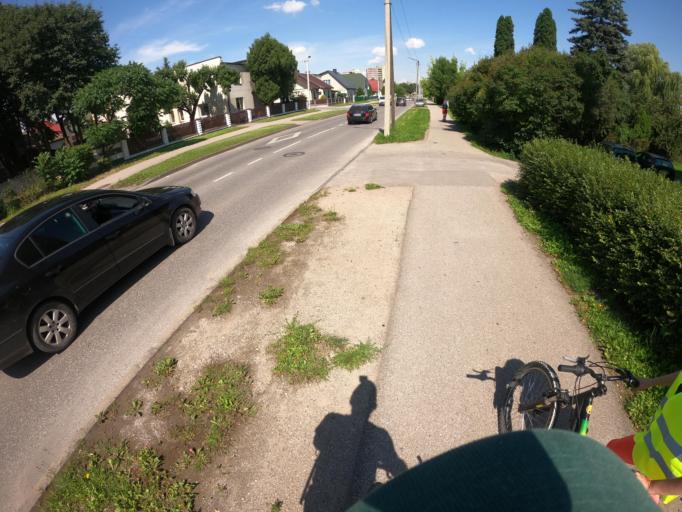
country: LT
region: Kauno apskritis
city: Dainava (Kaunas)
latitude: 54.9013
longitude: 23.9674
